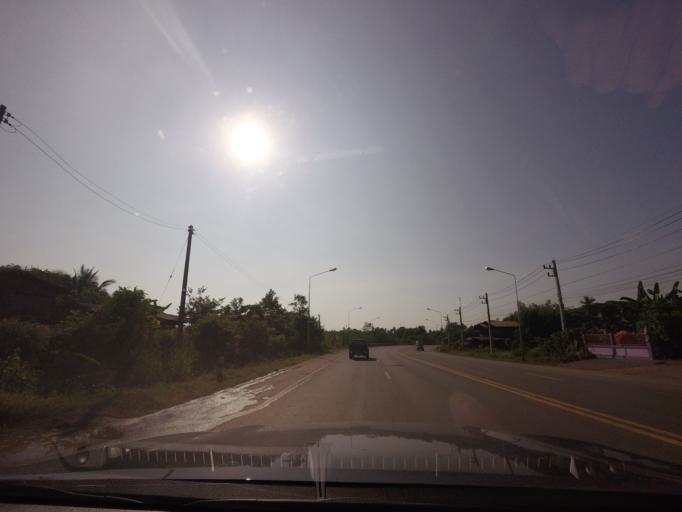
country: TH
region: Phetchabun
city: Lom Kao
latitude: 16.8387
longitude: 101.1813
